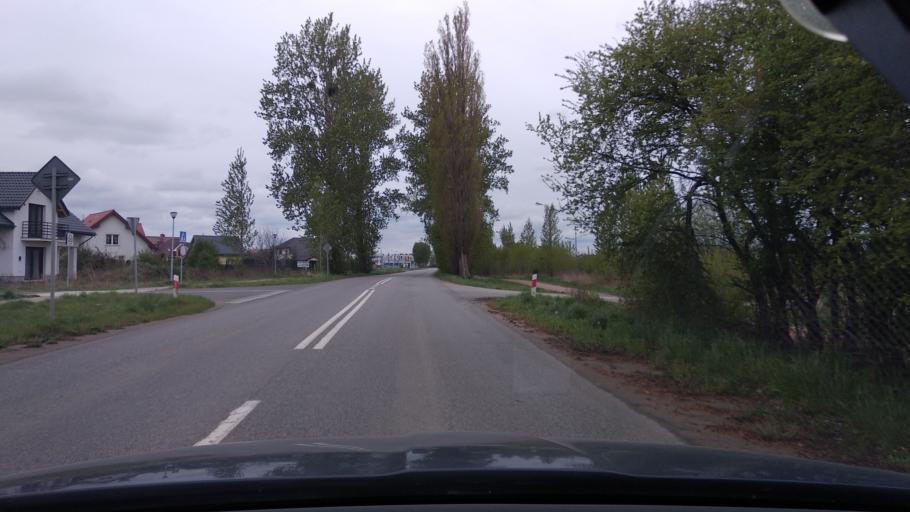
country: PL
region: Pomeranian Voivodeship
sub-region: Powiat gdanski
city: Pruszcz Gdanski
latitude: 54.2671
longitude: 18.6712
